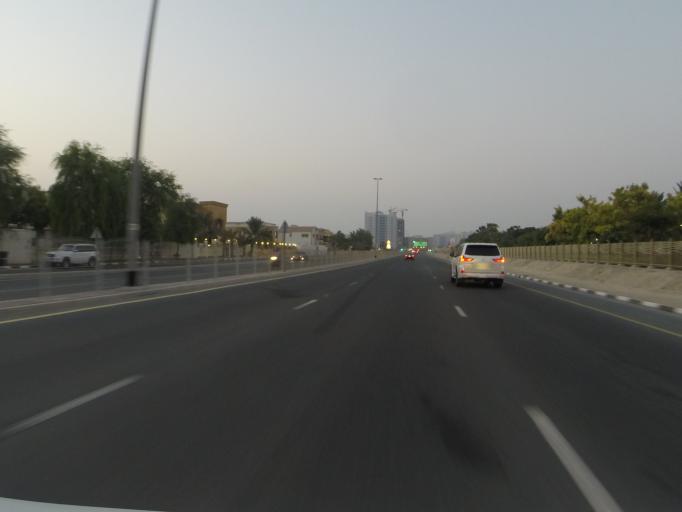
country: AE
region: Dubai
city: Dubai
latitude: 25.1001
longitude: 55.1997
